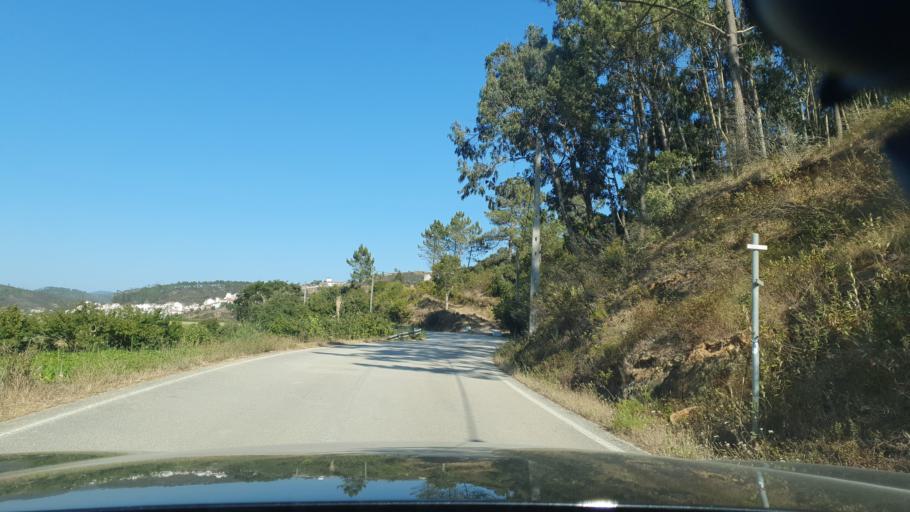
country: PT
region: Beja
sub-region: Odemira
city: Sao Teotonio
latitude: 37.4328
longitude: -8.7836
